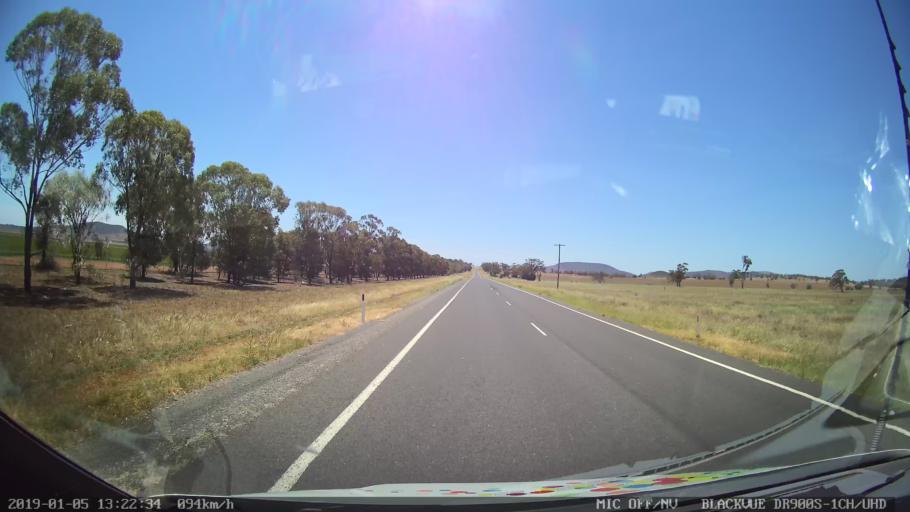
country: AU
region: New South Wales
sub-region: Gunnedah
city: Gunnedah
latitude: -31.0851
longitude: 149.9636
